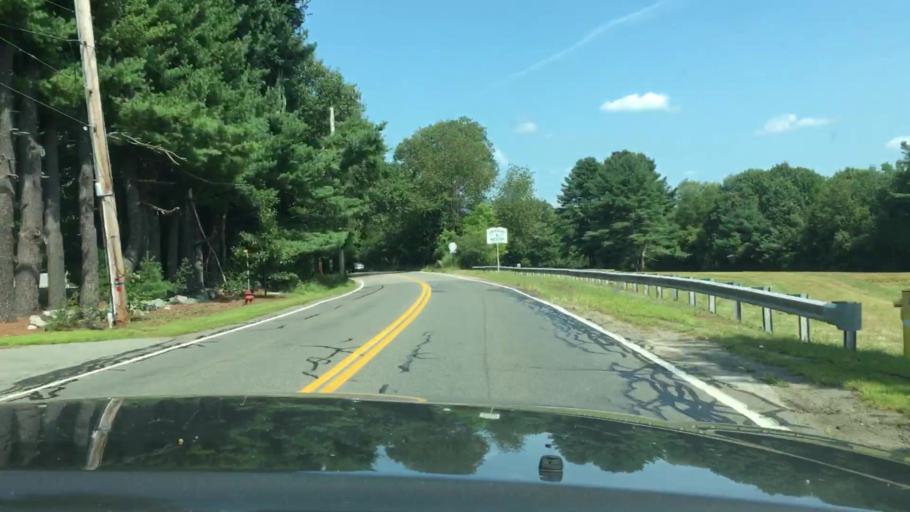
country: US
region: Massachusetts
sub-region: Middlesex County
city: Cochituate
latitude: 42.3297
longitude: -71.3292
